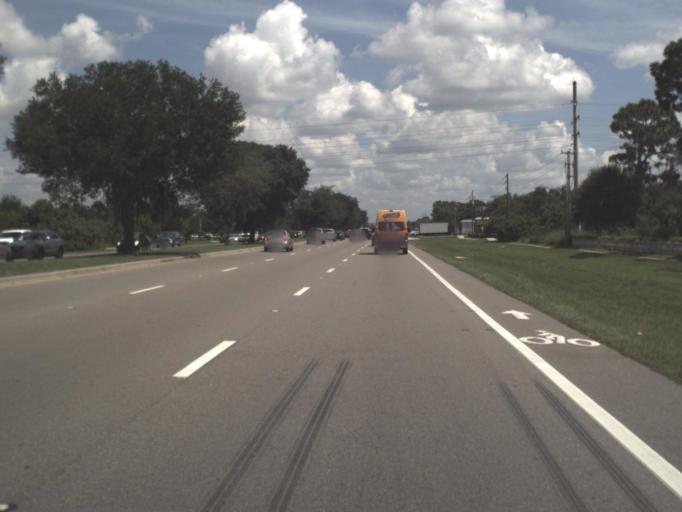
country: US
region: Florida
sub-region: Sarasota County
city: Desoto Lakes
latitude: 27.3882
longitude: -82.4698
